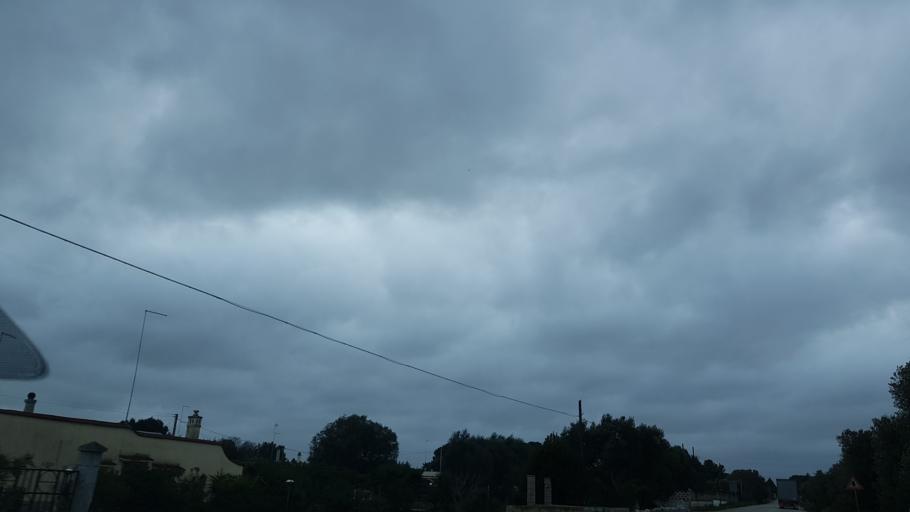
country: IT
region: Apulia
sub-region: Provincia di Brindisi
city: San Vito dei Normanni
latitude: 40.6541
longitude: 17.7740
